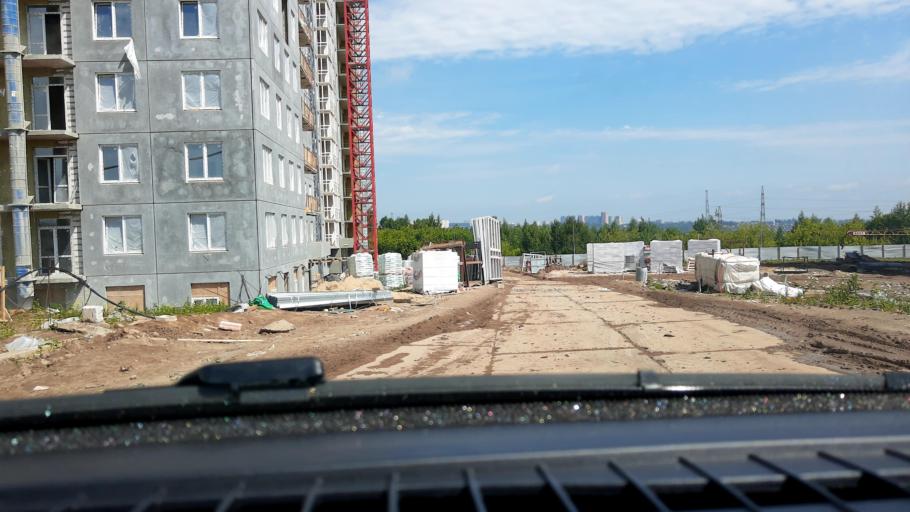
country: RU
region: Nizjnij Novgorod
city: Afonino
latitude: 56.2472
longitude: 44.0507
